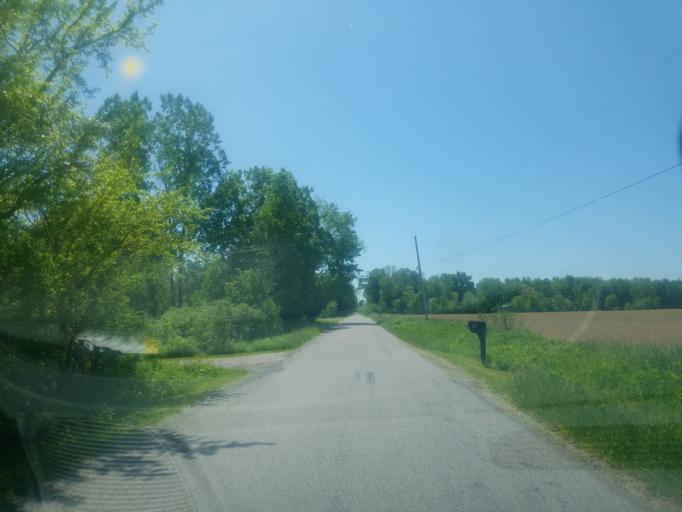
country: US
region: Ohio
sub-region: Huron County
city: Wakeman
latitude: 41.1950
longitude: -82.3702
